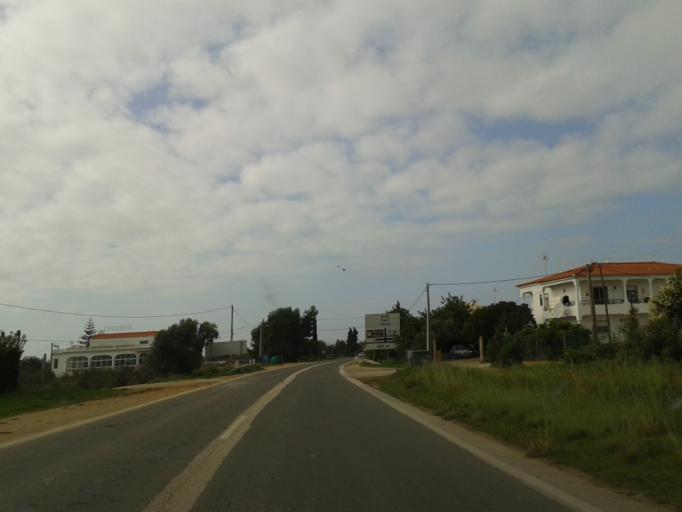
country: PT
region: Faro
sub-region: Vila Real de Santo Antonio
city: Monte Gordo
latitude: 37.1713
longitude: -7.5350
